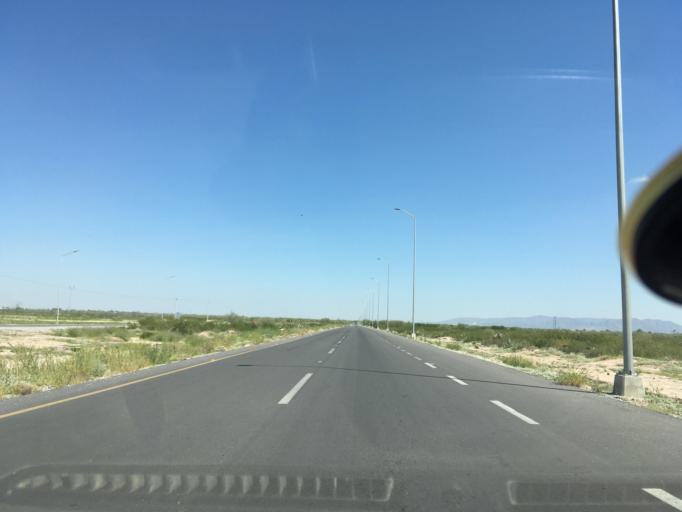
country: MX
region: Coahuila
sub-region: Torreon
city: Fraccionamiento la Noria
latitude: 25.4728
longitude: -103.3213
